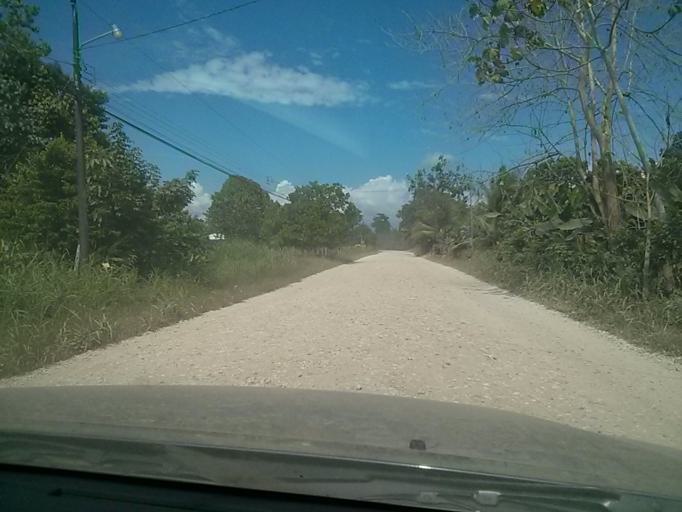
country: CR
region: Puntarenas
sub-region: Canton de Golfito
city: Golfito
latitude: 8.4569
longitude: -83.0493
